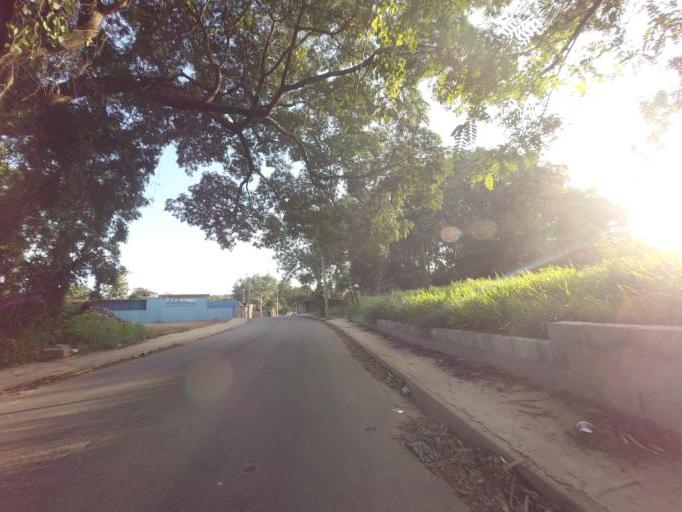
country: BR
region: Sao Paulo
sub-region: Piracicaba
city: Piracicaba
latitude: -22.7501
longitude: -47.6108
